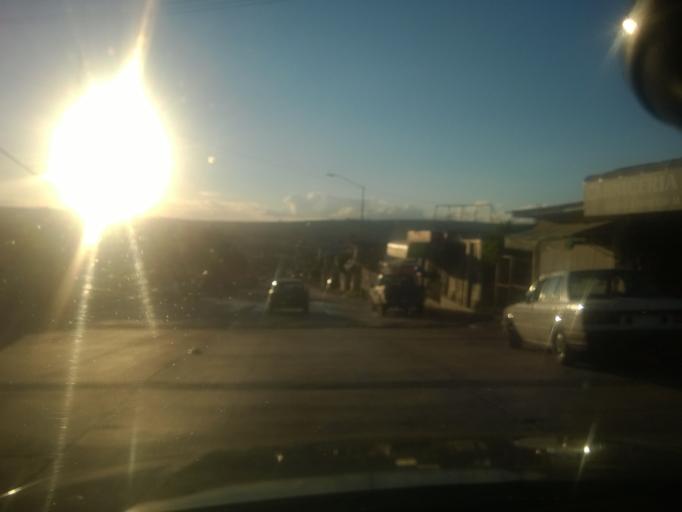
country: MX
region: Guanajuato
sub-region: Leon
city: La Ermita
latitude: 21.1534
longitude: -101.7348
